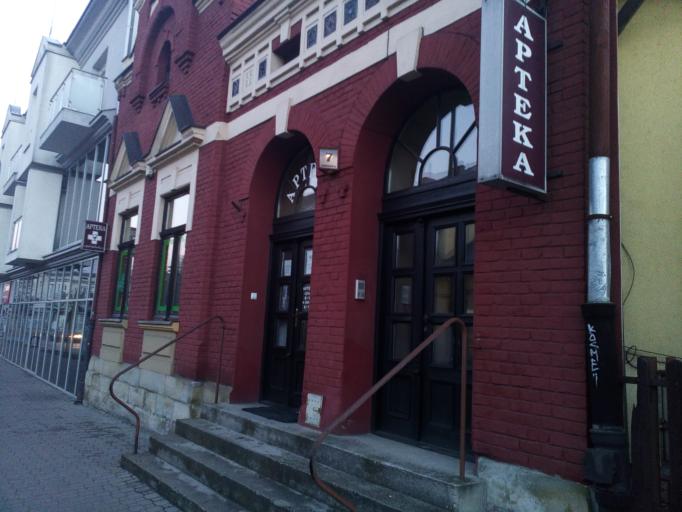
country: PL
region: Lesser Poland Voivodeship
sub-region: Powiat nowosadecki
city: Nowy Sacz
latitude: 49.6132
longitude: 20.6959
